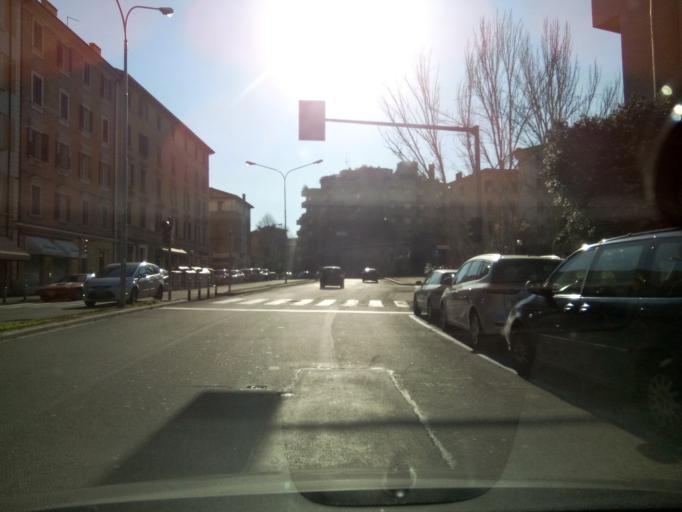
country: IT
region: Emilia-Romagna
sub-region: Provincia di Bologna
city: Bologna
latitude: 44.4974
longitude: 11.3178
